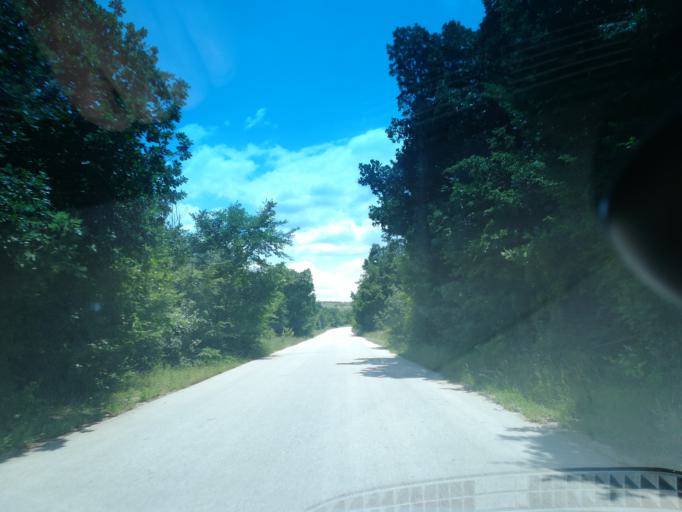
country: BG
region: Khaskovo
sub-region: Obshtina Mineralni Bani
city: Mineralni Bani
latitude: 41.9713
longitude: 25.2604
